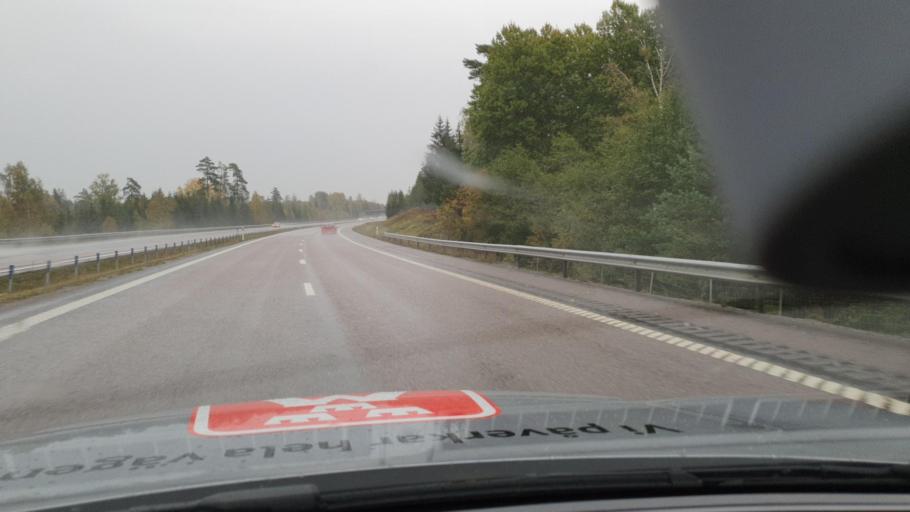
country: SE
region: OEstergoetland
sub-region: Norrkopings Kommun
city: Krokek
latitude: 58.7386
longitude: 16.4258
